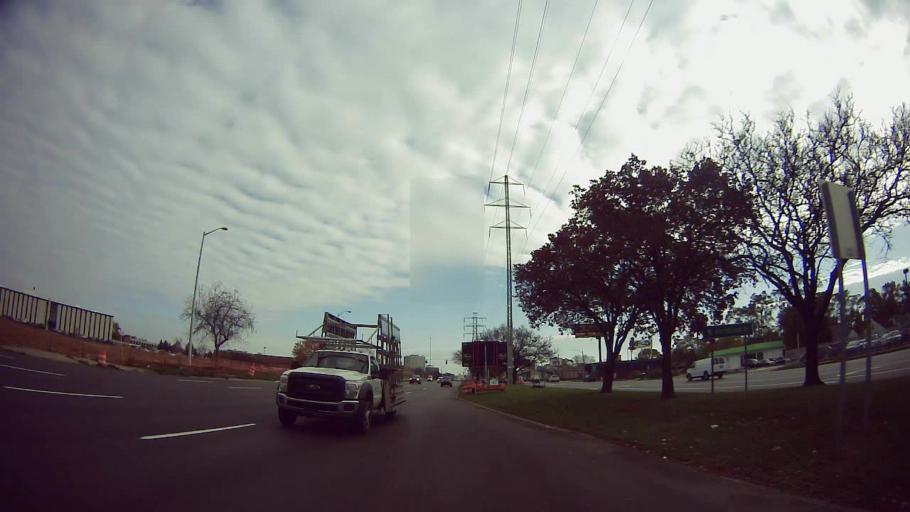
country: US
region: Michigan
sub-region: Oakland County
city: Southfield
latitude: 42.4446
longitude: -83.2120
